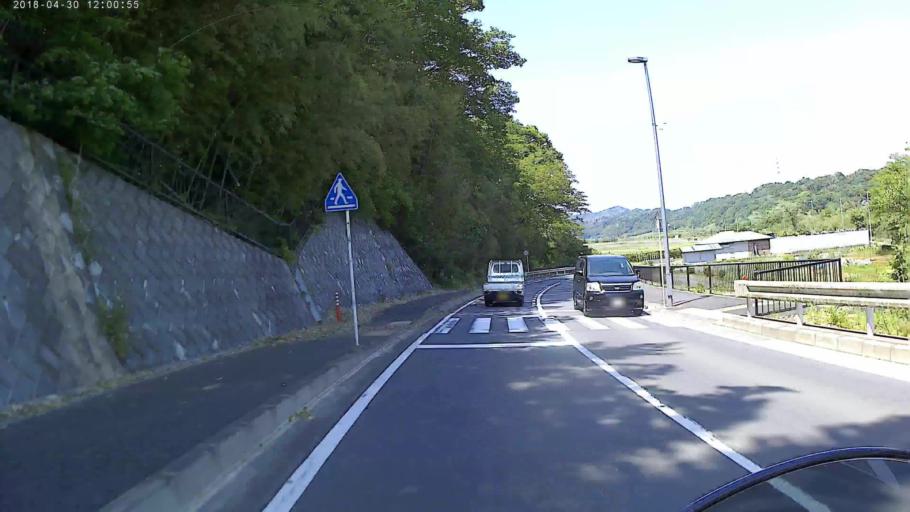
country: JP
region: Kanagawa
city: Zama
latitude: 35.5134
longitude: 139.3268
